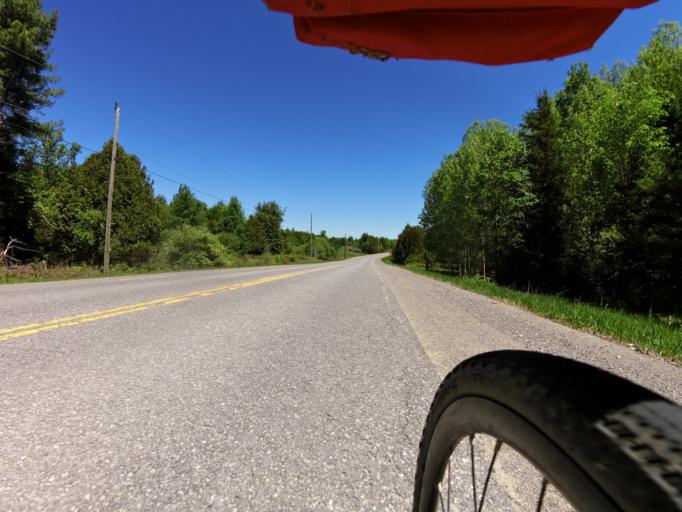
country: CA
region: Ontario
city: Carleton Place
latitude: 45.1836
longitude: -76.3829
